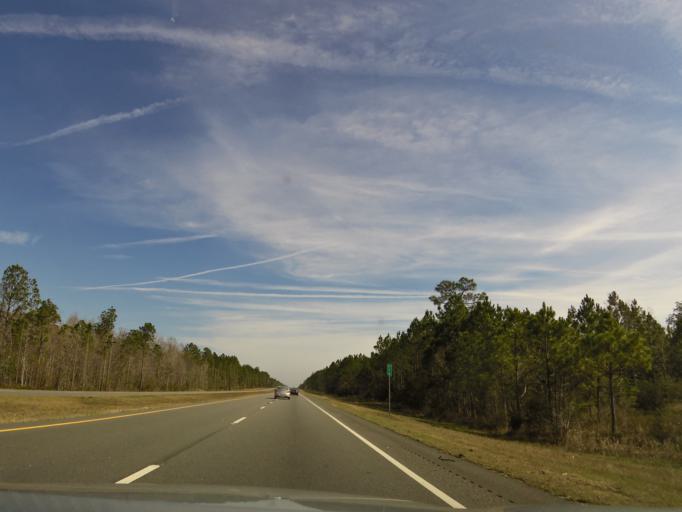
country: US
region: Georgia
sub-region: Brantley County
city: Nahunta
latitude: 31.2090
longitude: -81.9467
